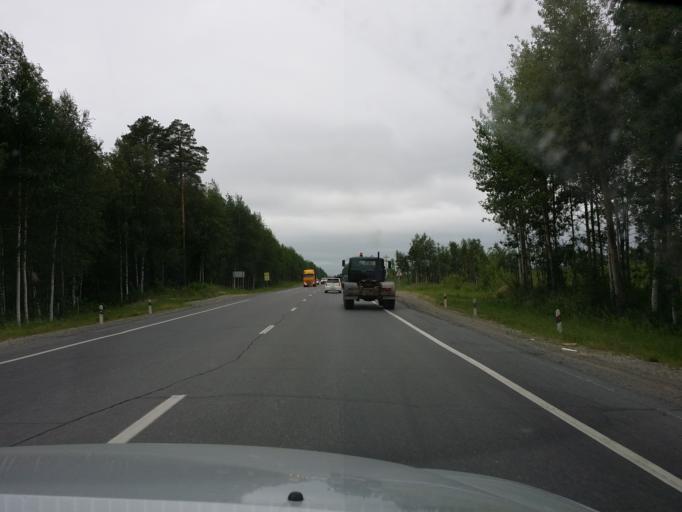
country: RU
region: Khanty-Mansiyskiy Avtonomnyy Okrug
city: Megion
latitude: 61.0616
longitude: 76.2785
